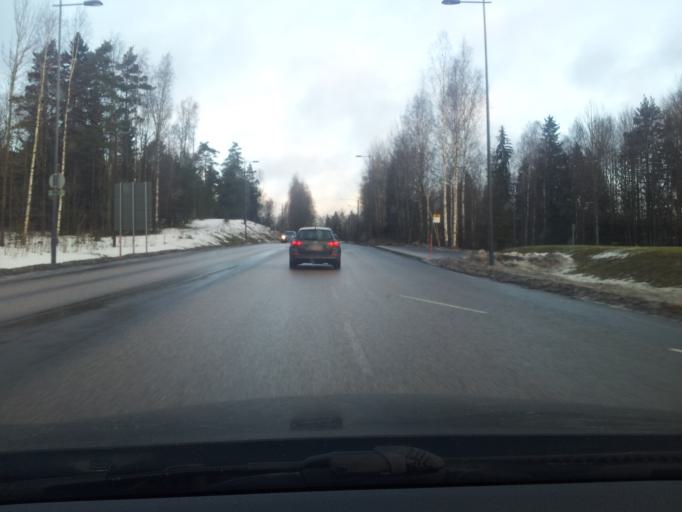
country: FI
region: Uusimaa
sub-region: Helsinki
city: Espoo
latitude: 60.1613
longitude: 24.6264
